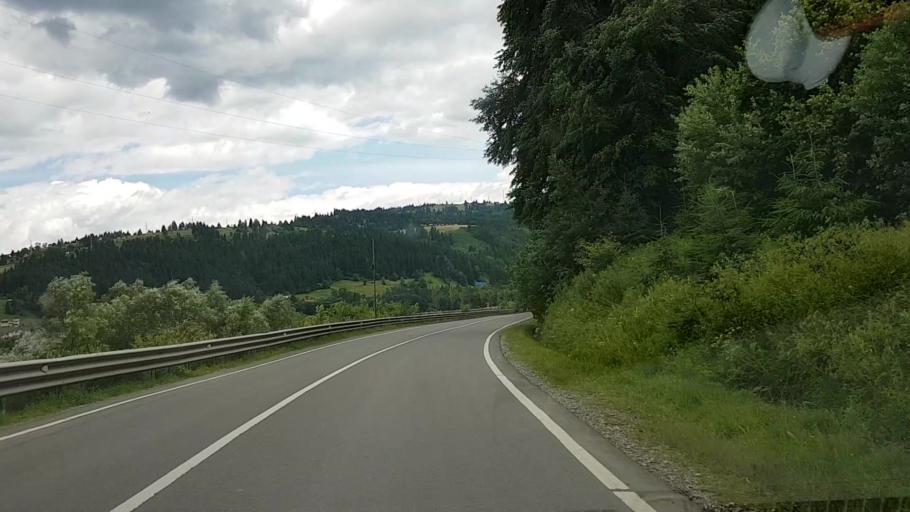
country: RO
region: Neamt
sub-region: Comuna Poiana Teiului
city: Poiana Teiului
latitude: 47.0910
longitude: 25.9581
